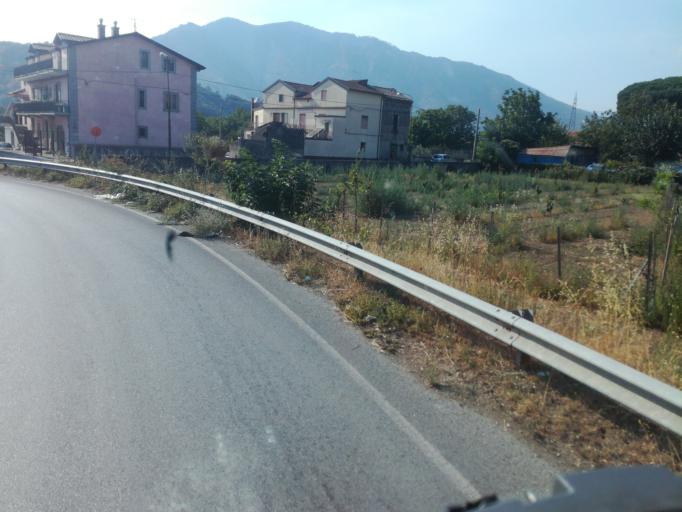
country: IT
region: Campania
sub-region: Provincia di Salerno
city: Piazza di Pandola
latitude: 40.7987
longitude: 14.7710
